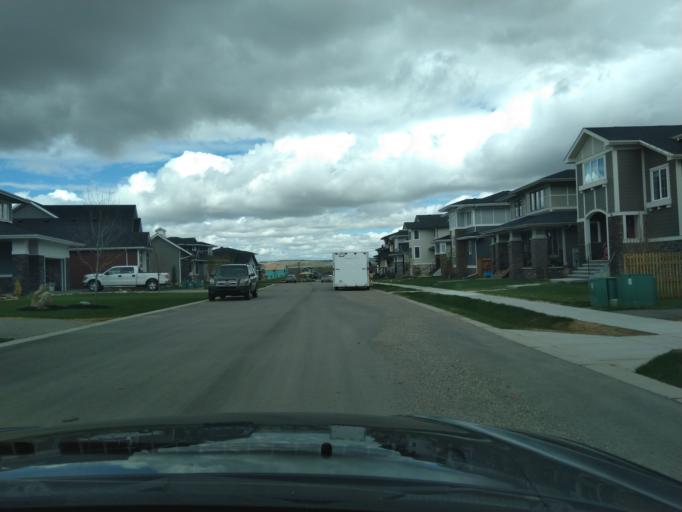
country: CA
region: Alberta
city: Cochrane
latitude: 51.1093
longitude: -114.3957
